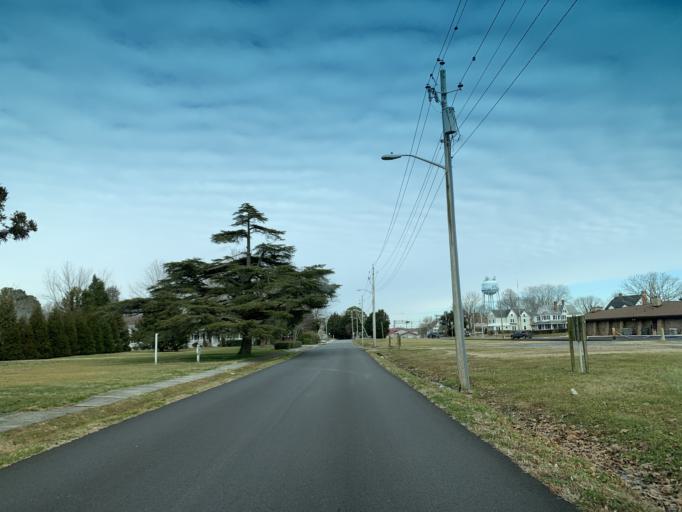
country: US
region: Maryland
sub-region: Worcester County
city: Berlin
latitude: 38.3287
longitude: -75.2216
